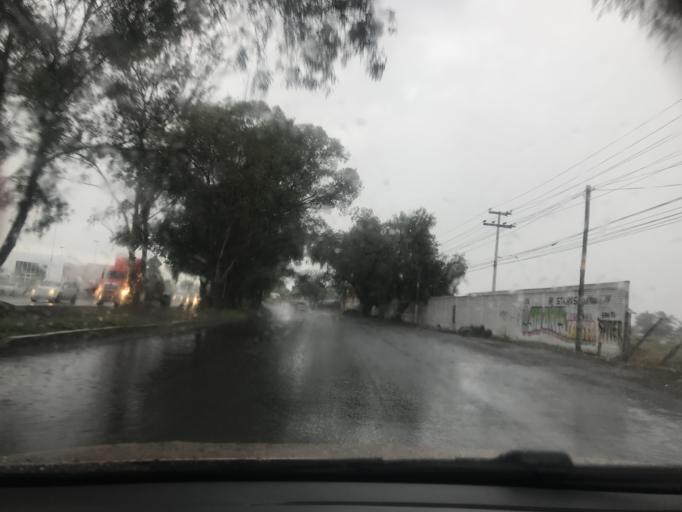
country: MX
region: Mexico
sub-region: Texcoco
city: Santa Martha
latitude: 19.4267
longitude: -98.9102
